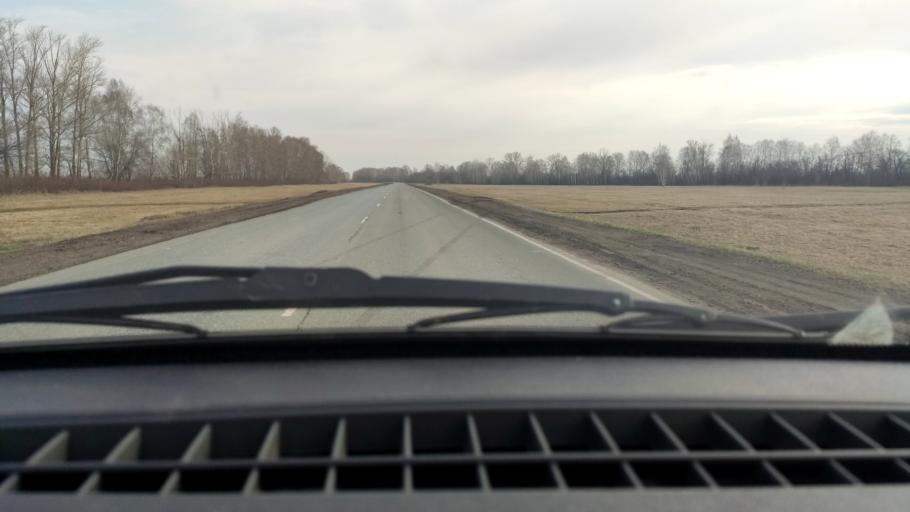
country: RU
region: Bashkortostan
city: Chishmy
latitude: 54.4045
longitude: 55.2157
